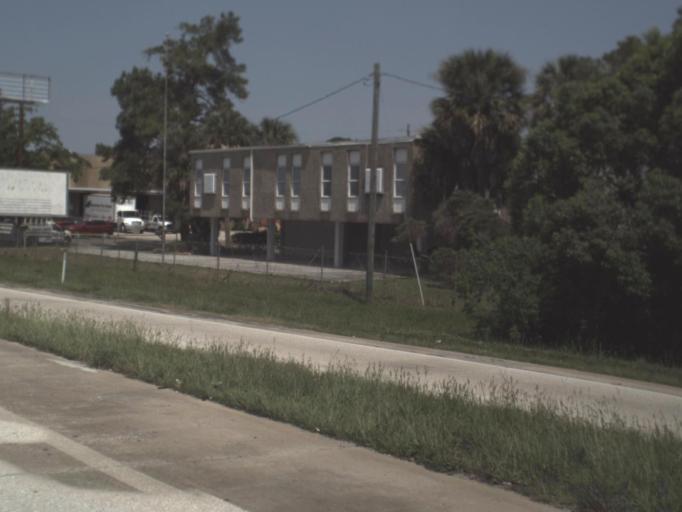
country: US
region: Florida
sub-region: Duval County
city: Jacksonville
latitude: 30.3156
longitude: -81.7540
